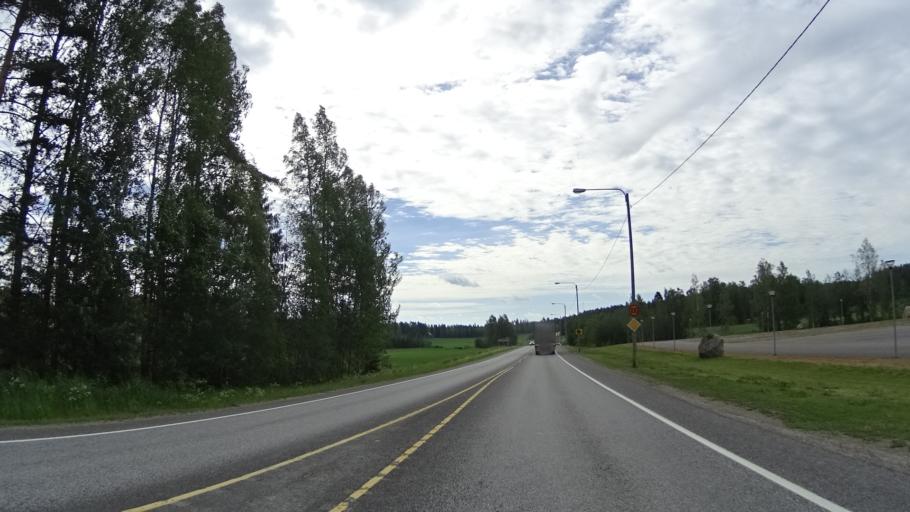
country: FI
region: Uusimaa
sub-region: Helsinki
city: Karkkila
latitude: 60.5169
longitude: 24.2479
